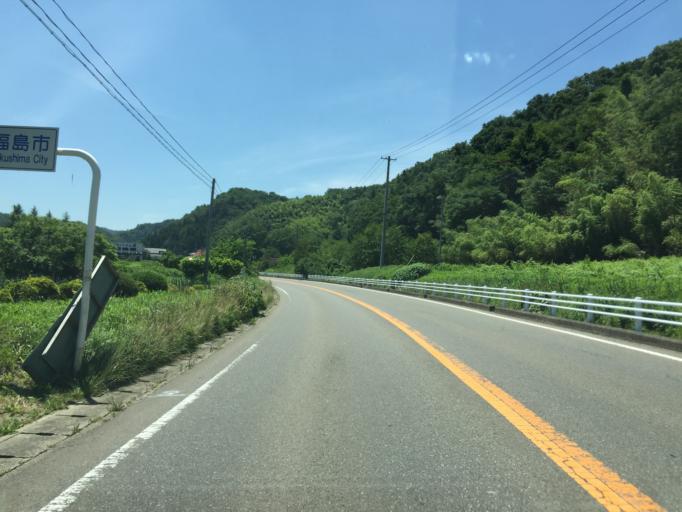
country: JP
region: Fukushima
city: Hobaramachi
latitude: 37.7655
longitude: 140.5674
